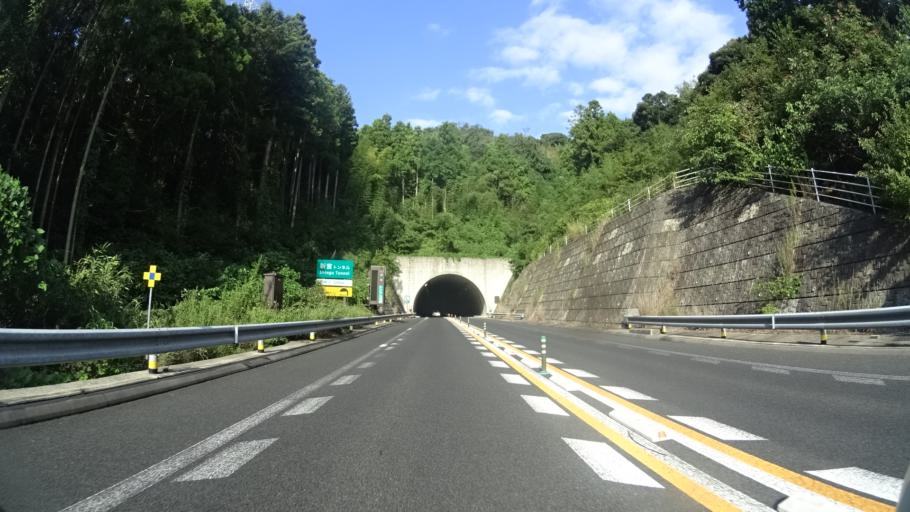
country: JP
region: Shimane
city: Izumo
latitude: 35.3257
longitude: 132.7430
